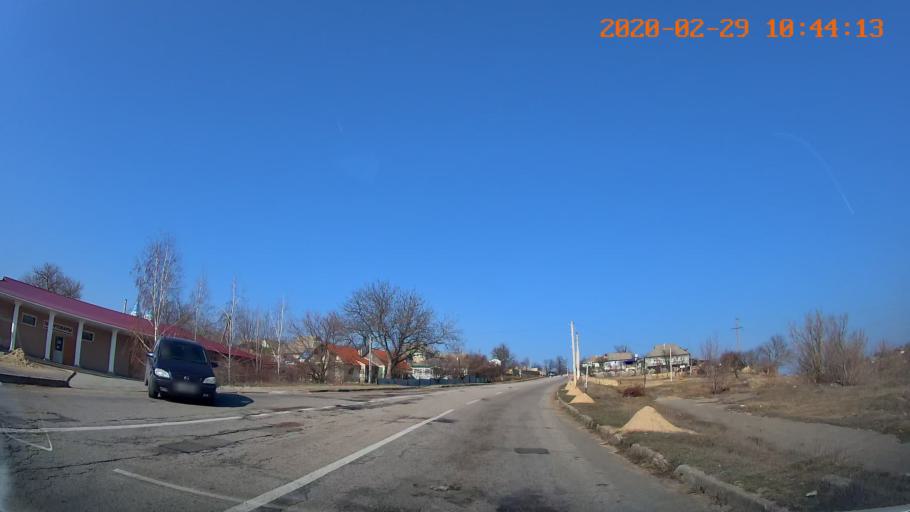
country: MD
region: Telenesti
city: Grigoriopol
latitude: 47.0684
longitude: 29.3970
